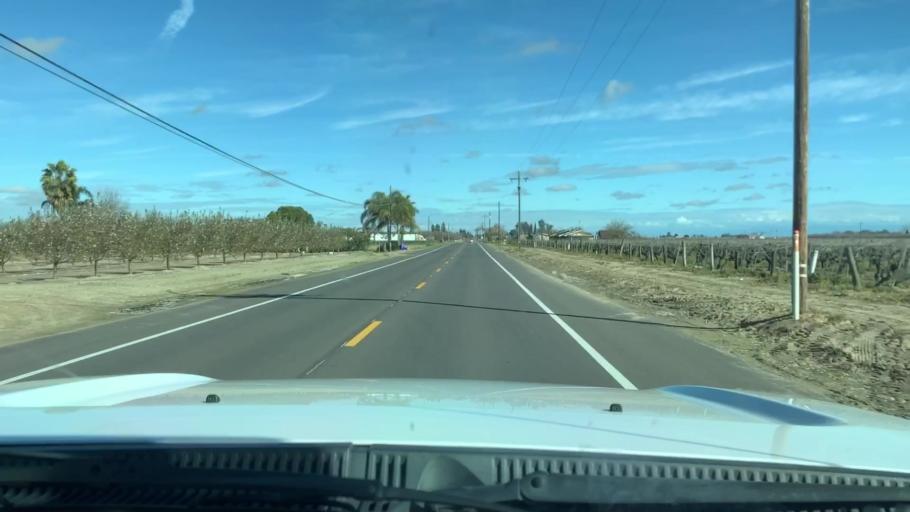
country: US
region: California
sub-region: Fresno County
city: Selma
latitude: 36.5382
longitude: -119.6828
